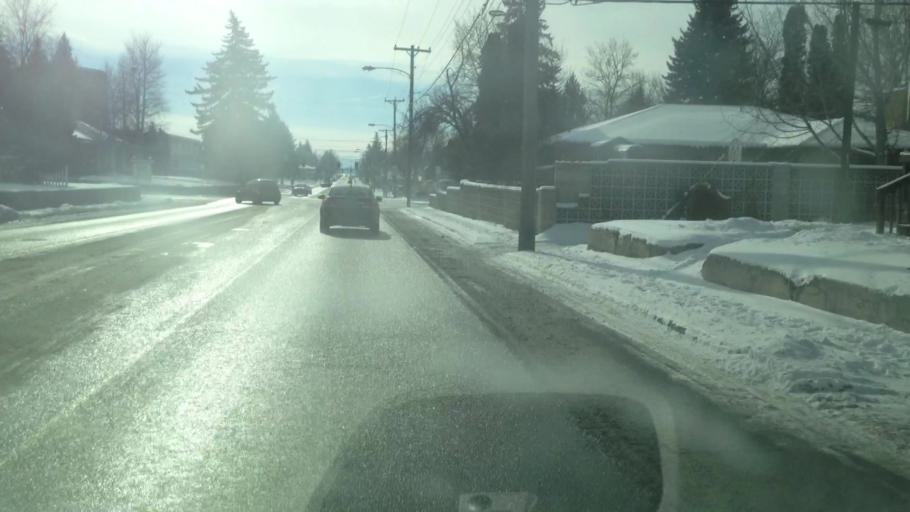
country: US
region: Idaho
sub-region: Bonneville County
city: Idaho Falls
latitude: 43.4948
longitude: -112.0239
